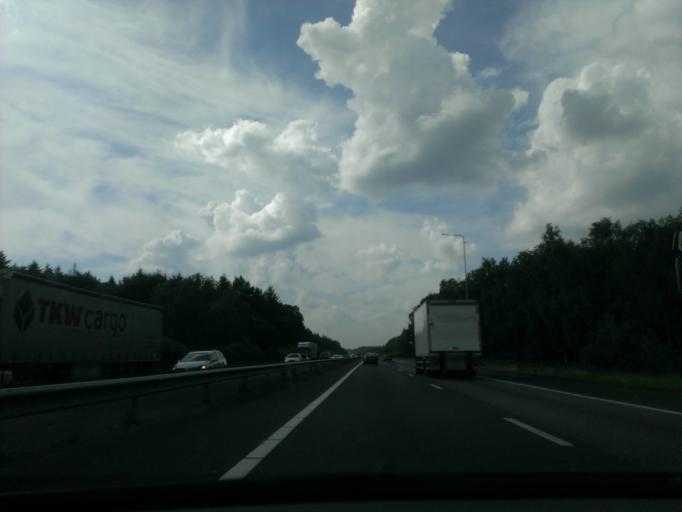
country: NL
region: Gelderland
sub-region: Gemeente Apeldoorn
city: Beekbergen
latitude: 52.1828
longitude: 5.9107
